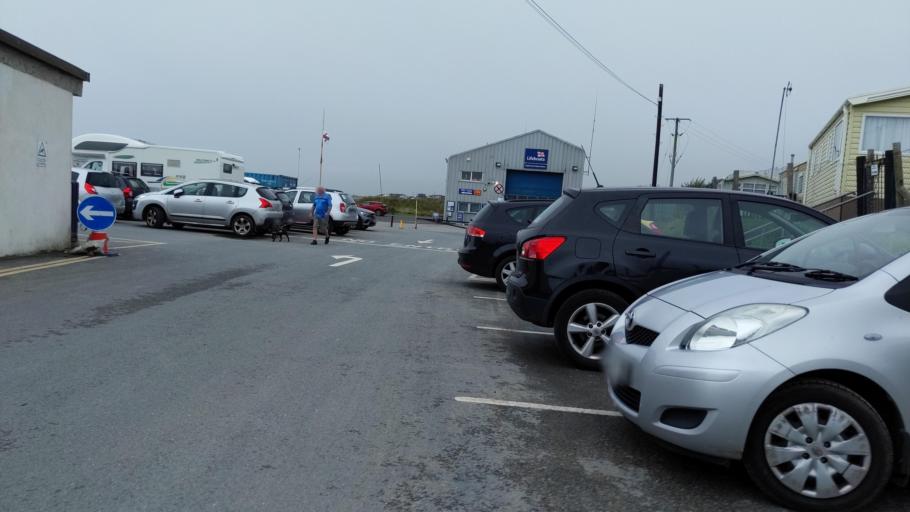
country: IE
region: Leinster
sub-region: Lu
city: Clogherhead
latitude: 53.7889
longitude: -6.2347
